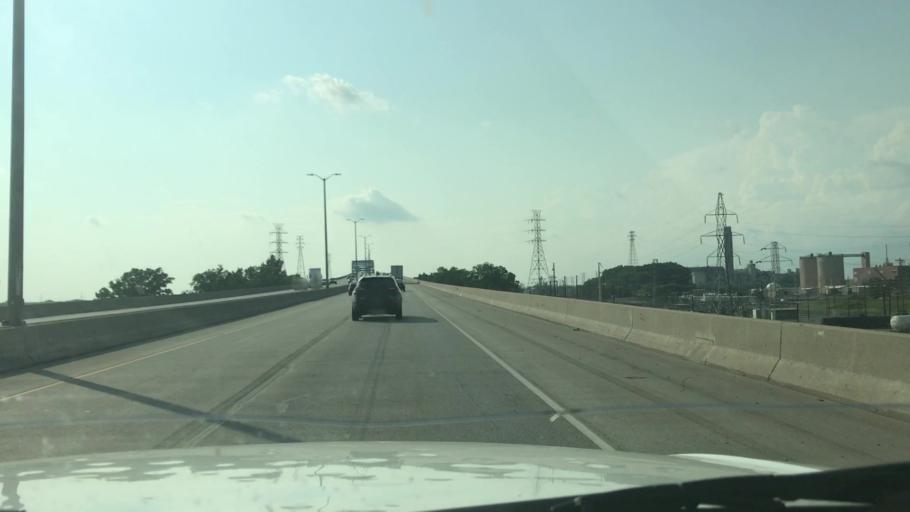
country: US
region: Wisconsin
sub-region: Brown County
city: Green Bay
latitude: 44.5291
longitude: -87.9942
